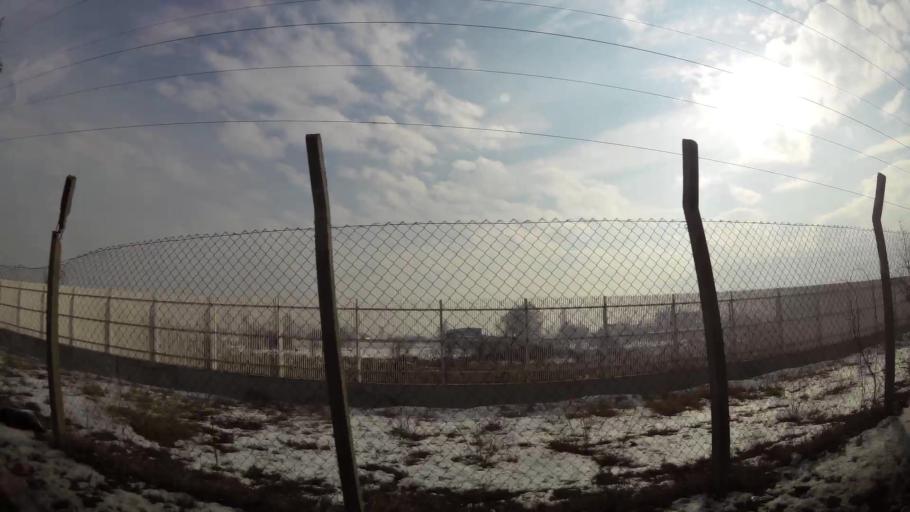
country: MK
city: Krushopek
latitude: 42.0170
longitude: 21.3660
